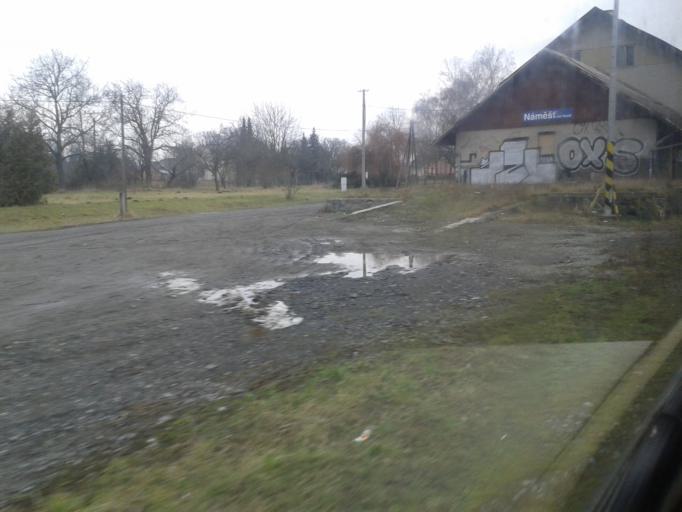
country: CZ
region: Olomoucky
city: Namest' na Hane
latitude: 49.5975
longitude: 17.0702
